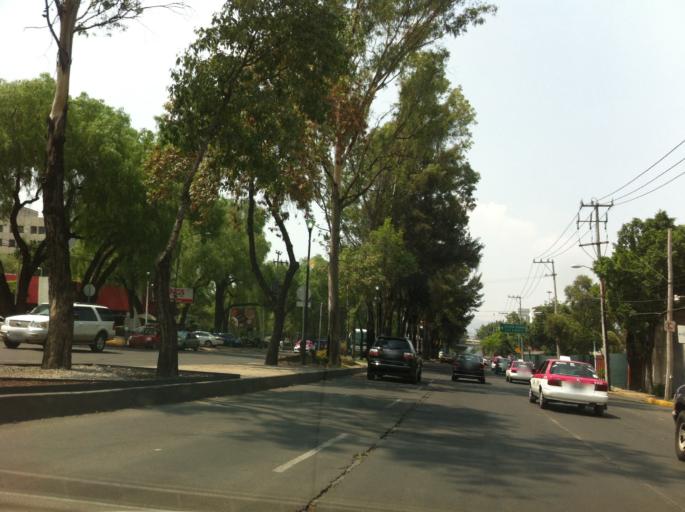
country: MX
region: Mexico
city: Colonia Lindavista
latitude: 19.4816
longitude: -99.1352
